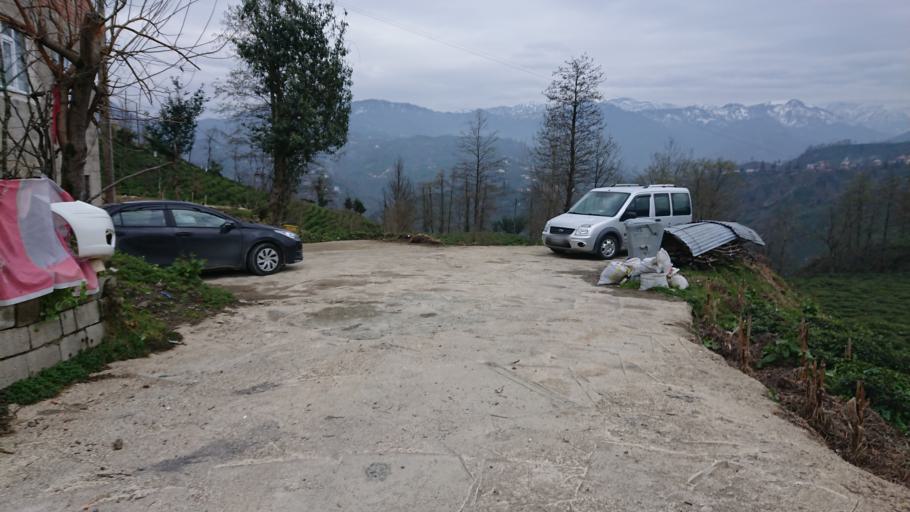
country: TR
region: Rize
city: Rize
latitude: 40.9704
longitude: 40.5179
